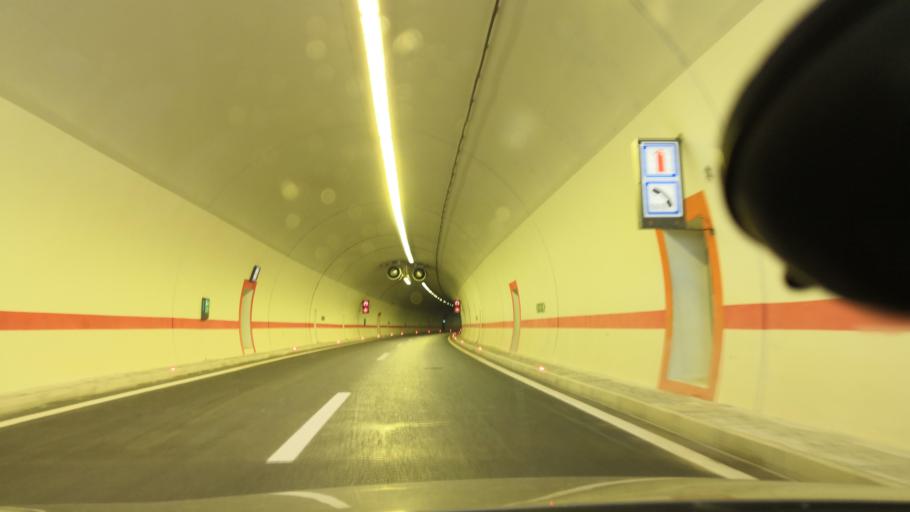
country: RS
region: Central Serbia
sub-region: Pcinjski Okrug
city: Vladicin Han
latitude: 42.7309
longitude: 22.0735
